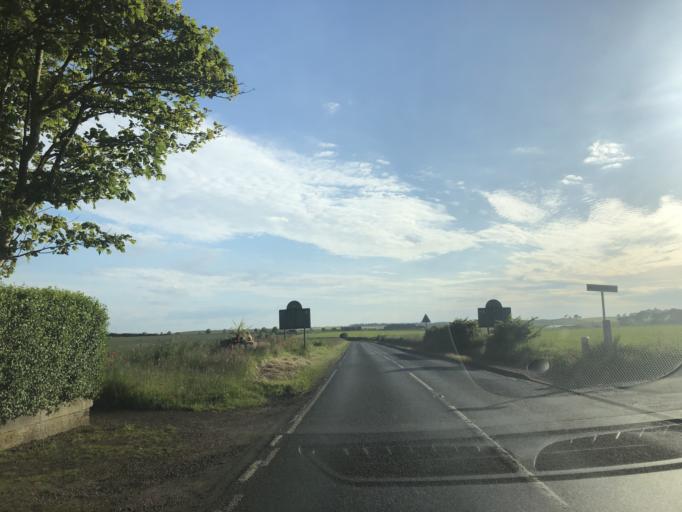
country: GB
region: Scotland
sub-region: Fife
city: Saint Monance
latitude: 56.2078
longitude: -2.7715
